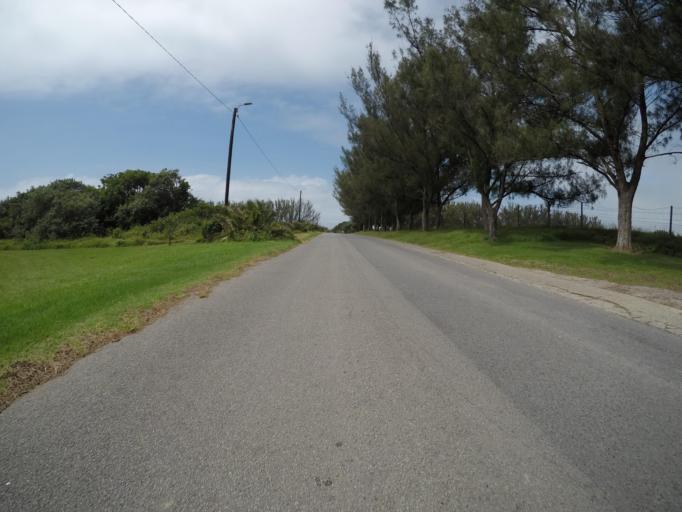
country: ZA
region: Eastern Cape
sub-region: Buffalo City Metropolitan Municipality
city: East London
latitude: -32.9389
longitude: 28.0256
